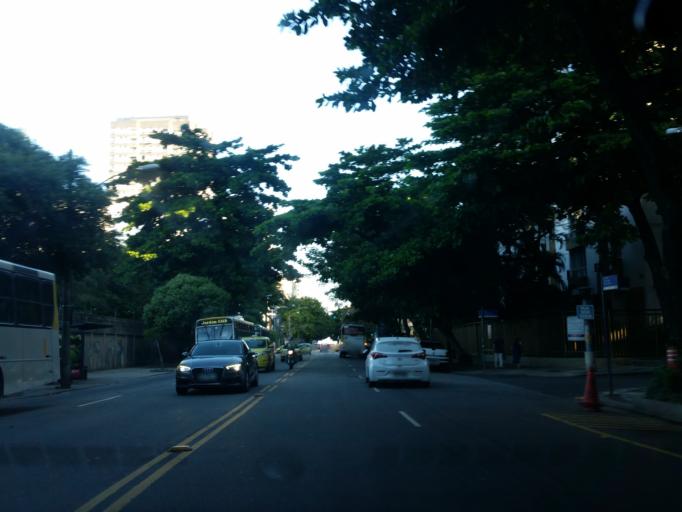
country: BR
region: Rio de Janeiro
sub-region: Rio De Janeiro
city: Rio de Janeiro
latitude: -22.9805
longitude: -43.2182
